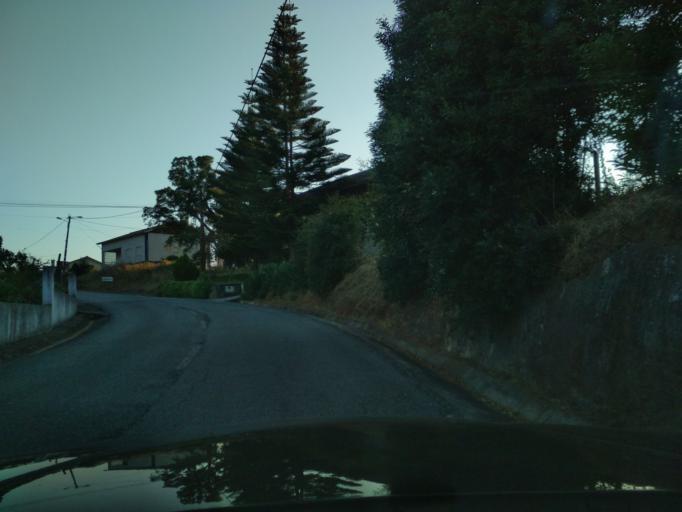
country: PT
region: Coimbra
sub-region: Coimbra
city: Coimbra
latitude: 40.2420
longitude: -8.4039
